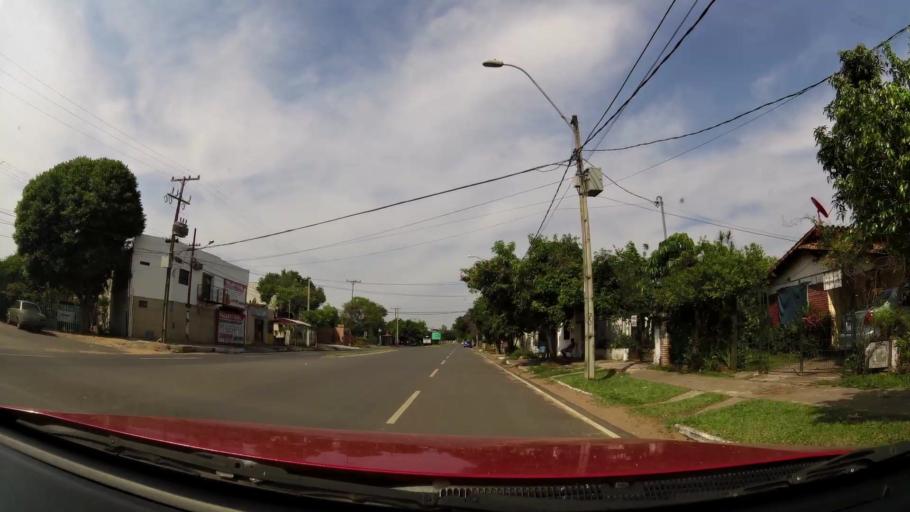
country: PY
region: Central
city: Fernando de la Mora
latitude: -25.2741
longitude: -57.5495
